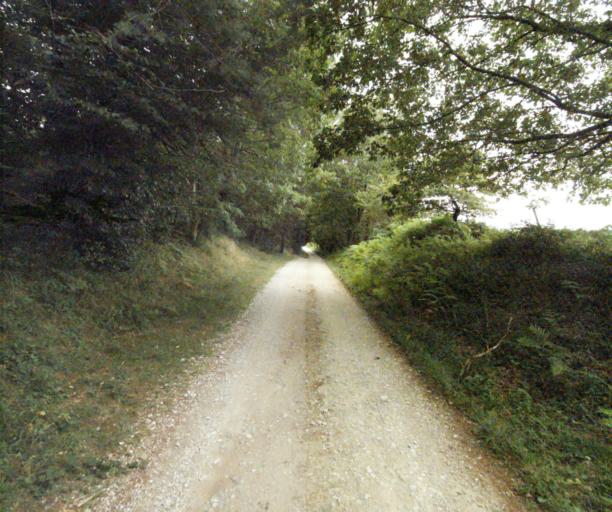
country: FR
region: Midi-Pyrenees
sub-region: Departement du Tarn
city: Soreze
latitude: 43.4285
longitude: 2.1083
